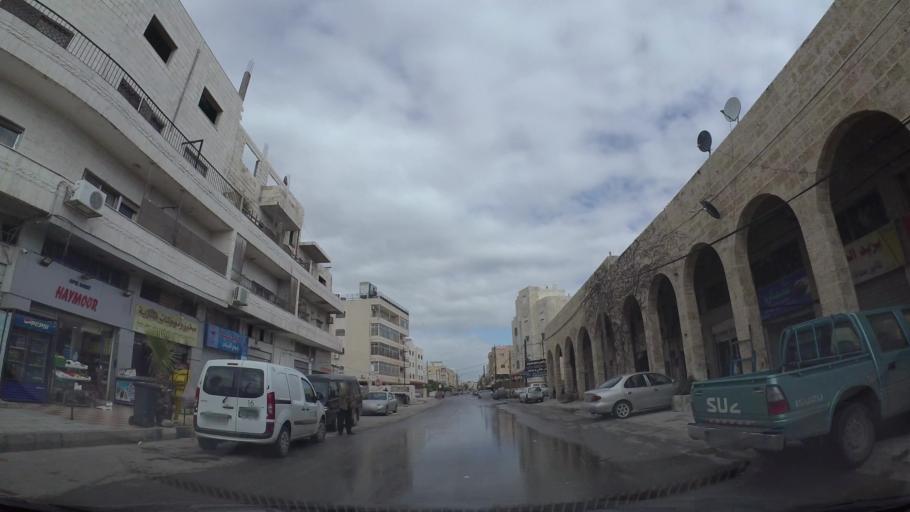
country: JO
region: Amman
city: Wadi as Sir
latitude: 31.9465
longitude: 35.8367
